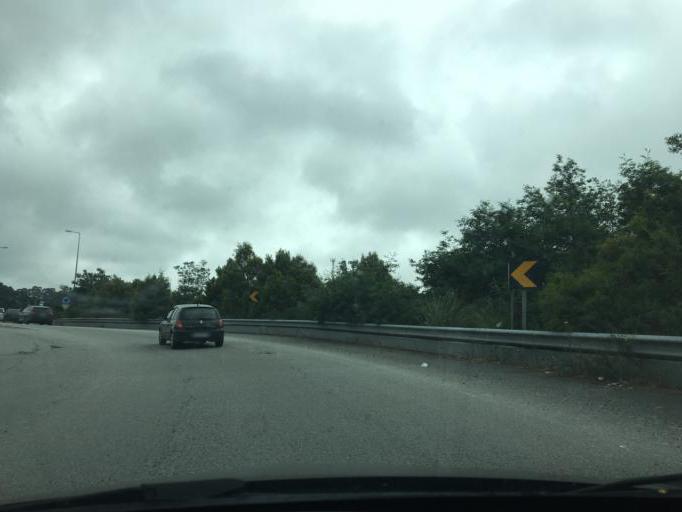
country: PT
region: Porto
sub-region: Matosinhos
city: Santa Cruz do Bispo
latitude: 41.2227
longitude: -8.6667
